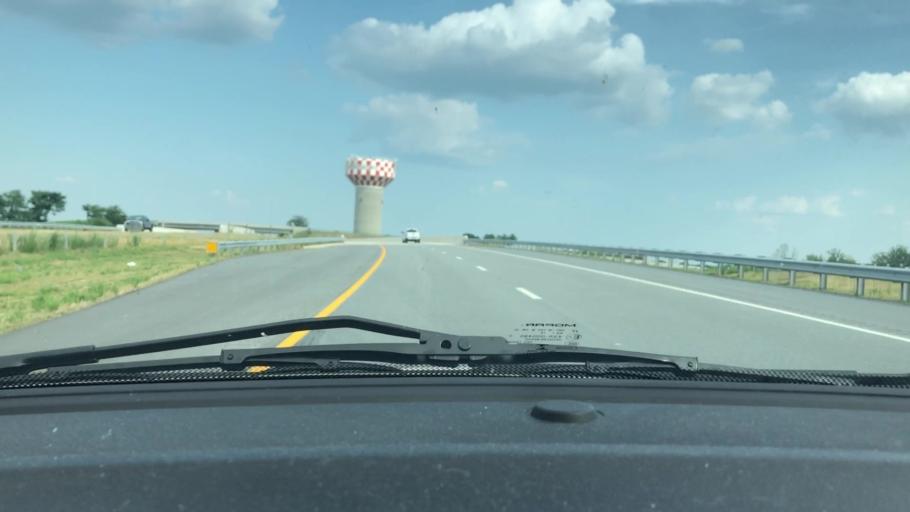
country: US
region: North Carolina
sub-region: Guilford County
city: Oak Ridge
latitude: 36.1251
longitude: -79.9635
